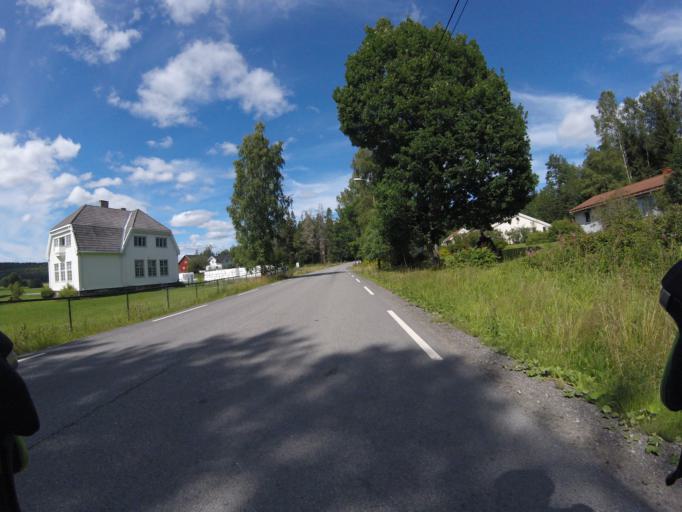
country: NO
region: Akershus
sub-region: Lorenskog
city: Kjenn
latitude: 59.9001
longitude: 10.9689
